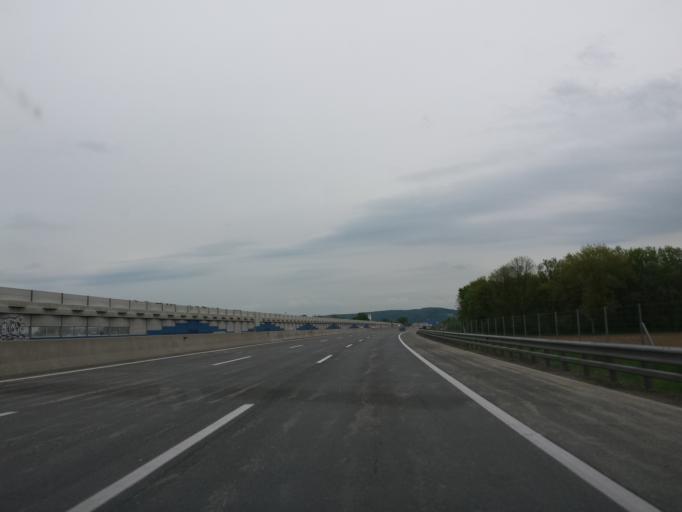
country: AT
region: Lower Austria
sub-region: Politischer Bezirk Korneuburg
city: Leobendorf
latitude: 48.3670
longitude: 16.2973
